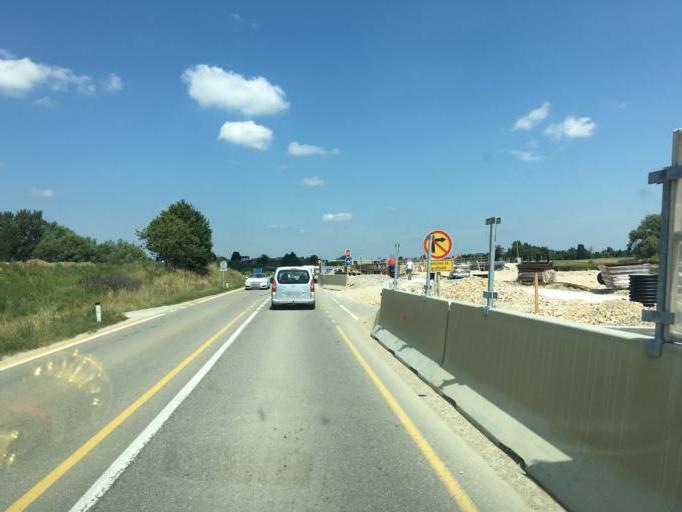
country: SI
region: Podlehnik
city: Podlehnik
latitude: 46.3518
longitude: 15.8680
